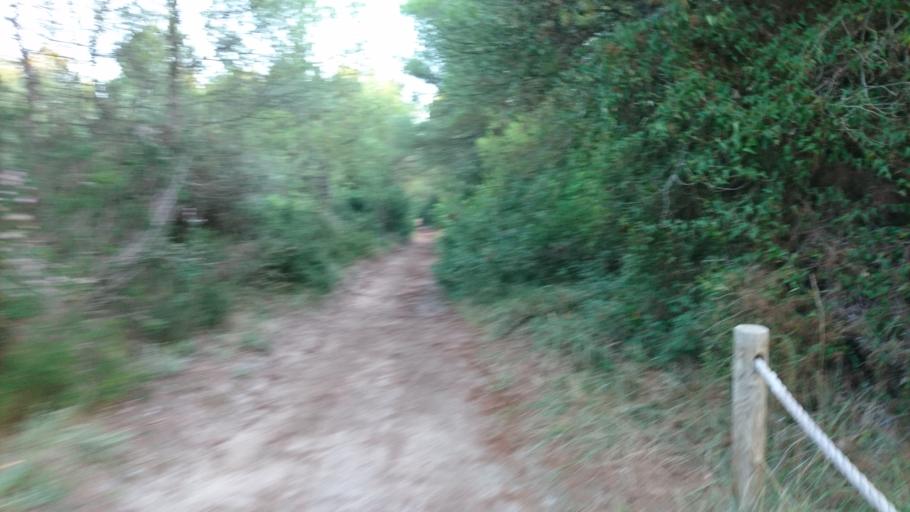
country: ES
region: Balearic Islands
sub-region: Illes Balears
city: Port d'Alcudia
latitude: 39.7837
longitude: 3.1305
